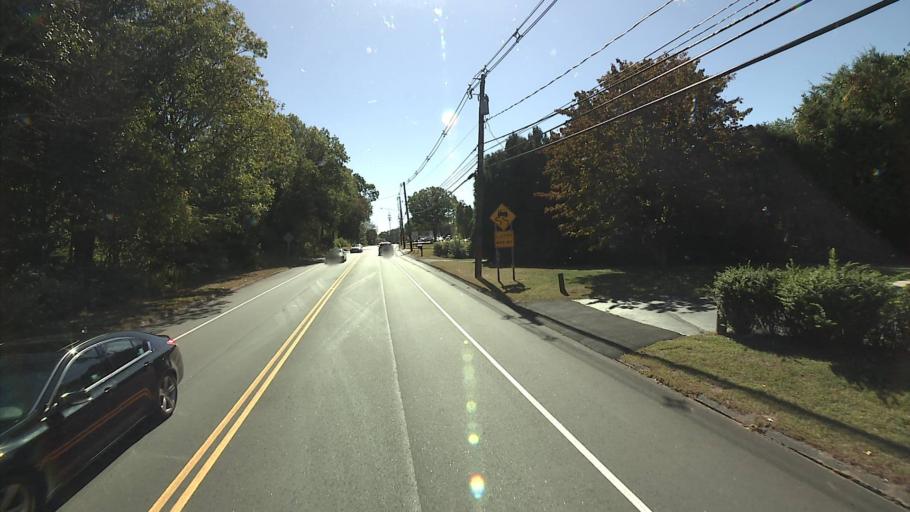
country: US
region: Connecticut
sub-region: New Haven County
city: Prospect
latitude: 41.5160
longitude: -72.9874
